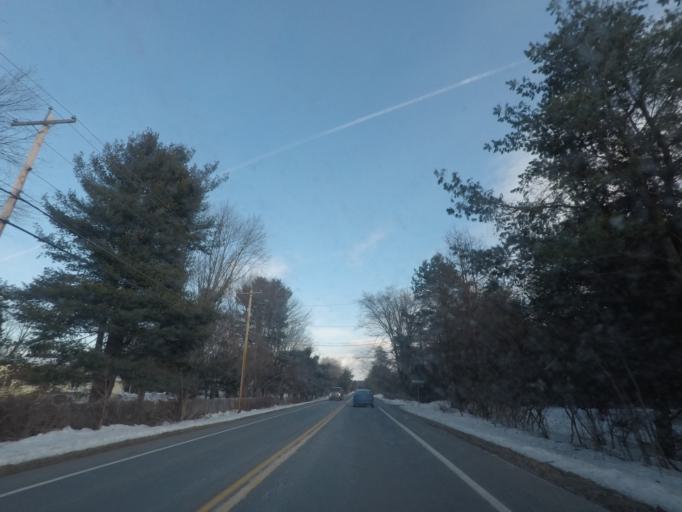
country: US
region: New York
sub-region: Schenectady County
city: Niskayuna
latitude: 42.8402
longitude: -73.8047
